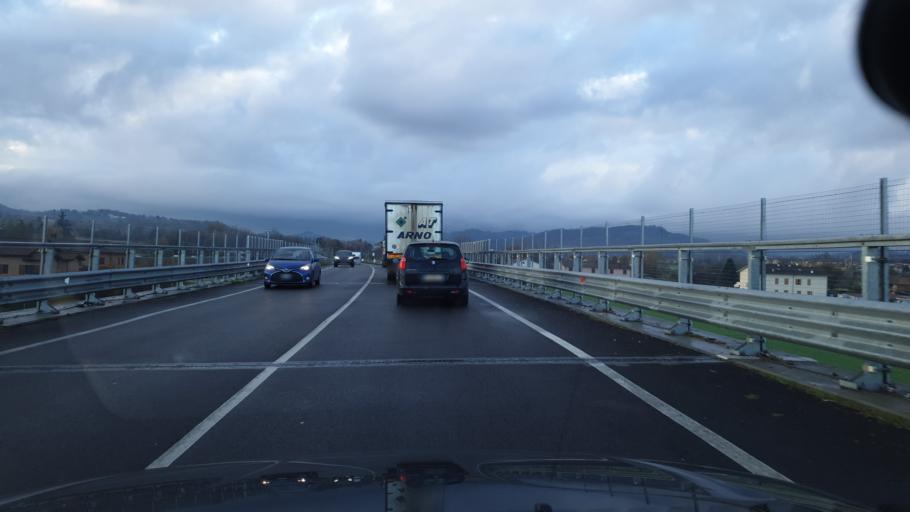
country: IT
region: Emilia-Romagna
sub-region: Provincia di Bologna
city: Bazzano
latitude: 44.5114
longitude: 11.1049
